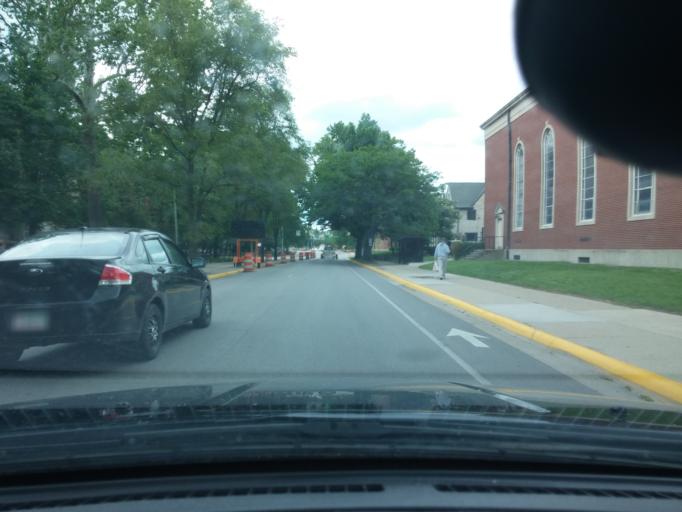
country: US
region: Indiana
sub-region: Tippecanoe County
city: West Lafayette
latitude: 40.4258
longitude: -86.9104
